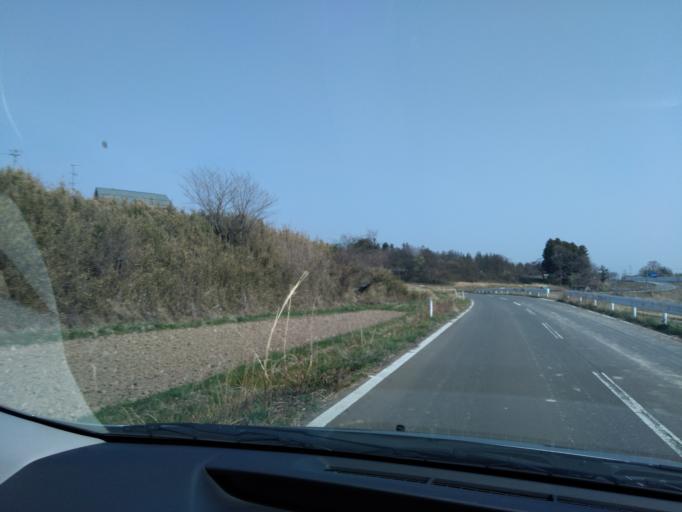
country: JP
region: Miyagi
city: Kogota
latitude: 38.7349
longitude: 141.0783
